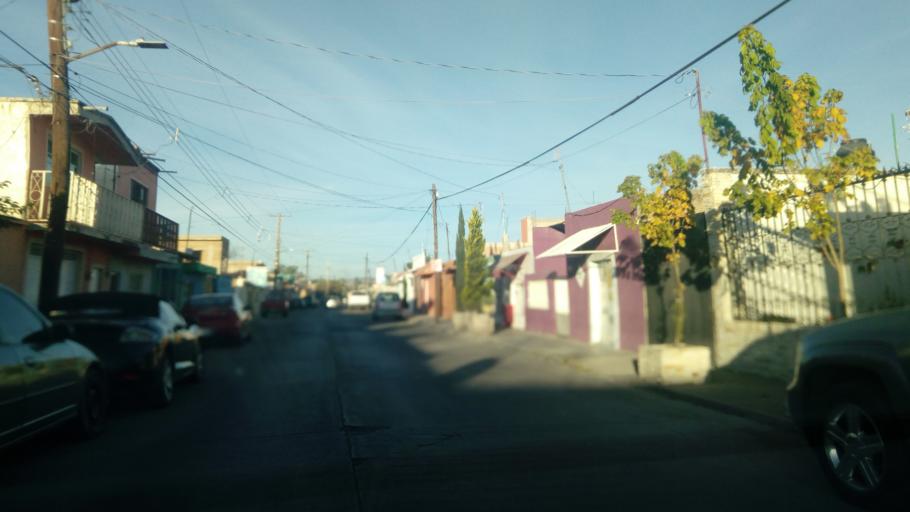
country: MX
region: Durango
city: Victoria de Durango
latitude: 24.0025
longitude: -104.6561
